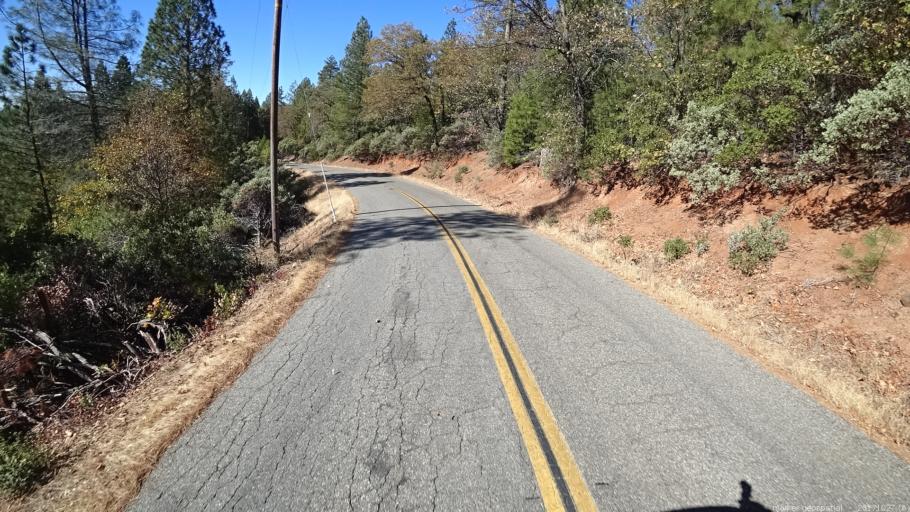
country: US
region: California
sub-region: Shasta County
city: Bella Vista
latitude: 40.7224
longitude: -122.0200
